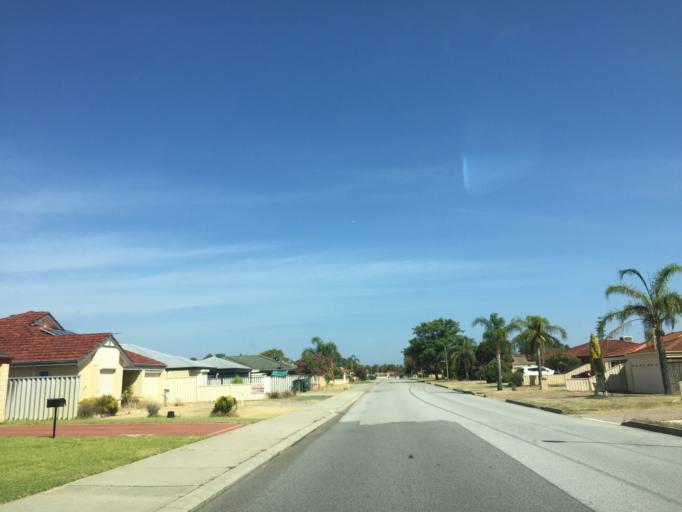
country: AU
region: Western Australia
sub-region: Gosnells
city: Thornlie
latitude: -32.0805
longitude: 115.9599
